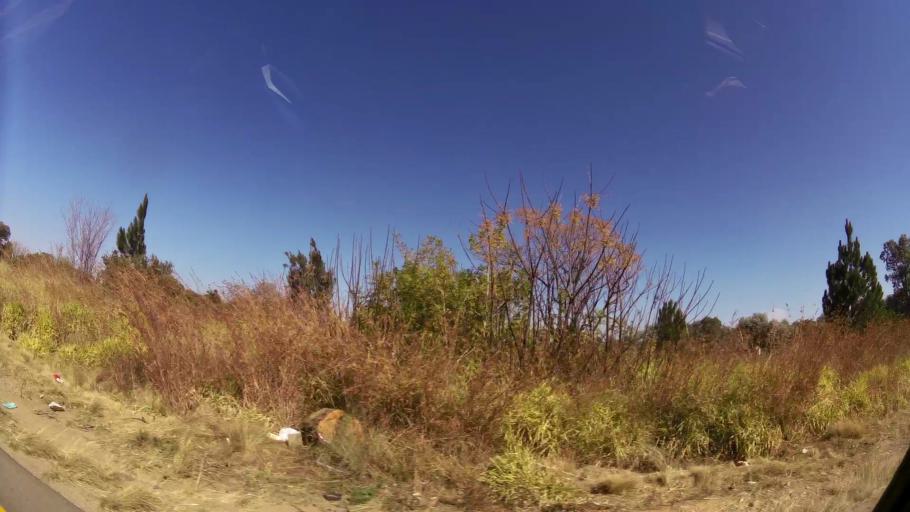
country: ZA
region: Gauteng
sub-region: City of Johannesburg Metropolitan Municipality
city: Midrand
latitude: -25.9372
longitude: 28.0898
